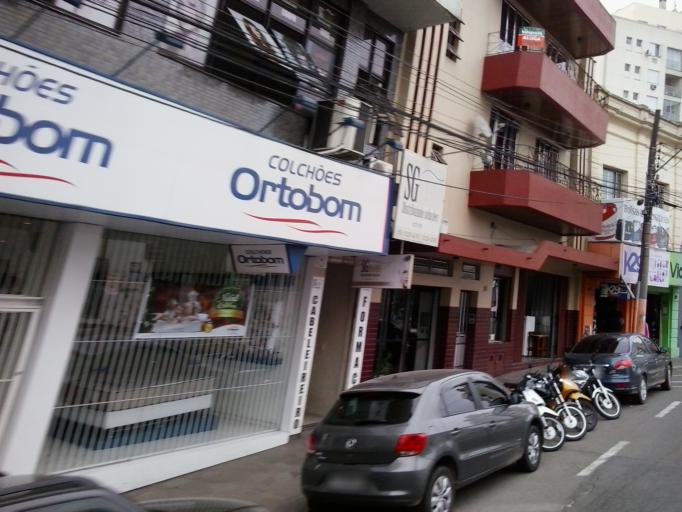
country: BR
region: Rio Grande do Sul
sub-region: Santa Maria
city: Santa Maria
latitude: -29.6898
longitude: -53.8025
